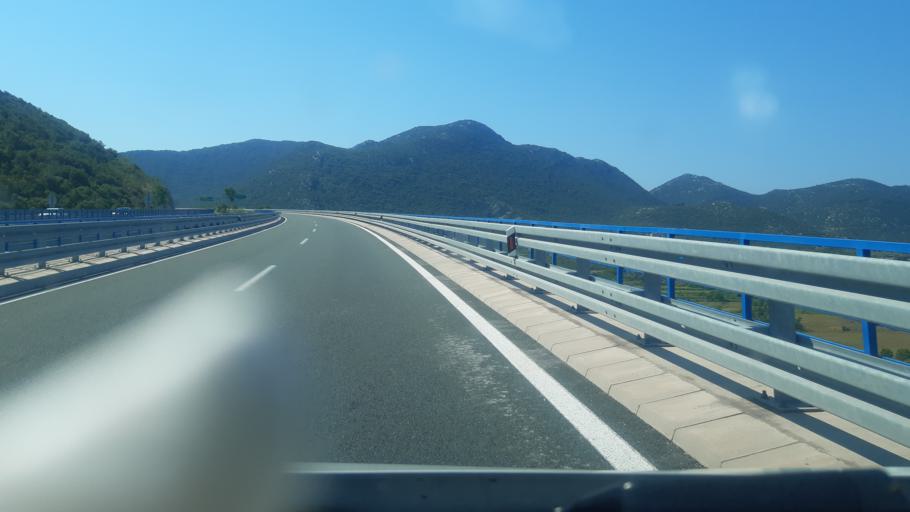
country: HR
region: Dubrovacko-Neretvanska
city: Komin
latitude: 43.1096
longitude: 17.4783
